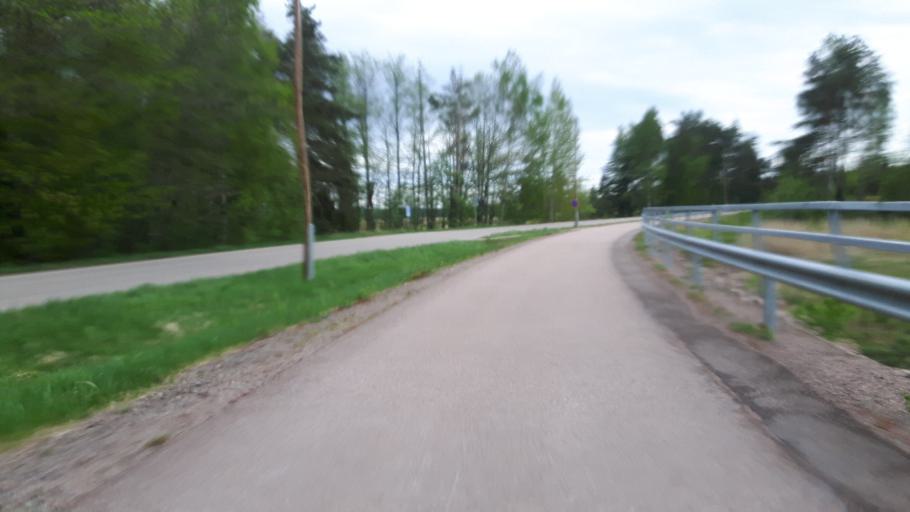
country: FI
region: Kymenlaakso
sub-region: Kotka-Hamina
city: Hamina
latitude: 60.5526
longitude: 27.2293
